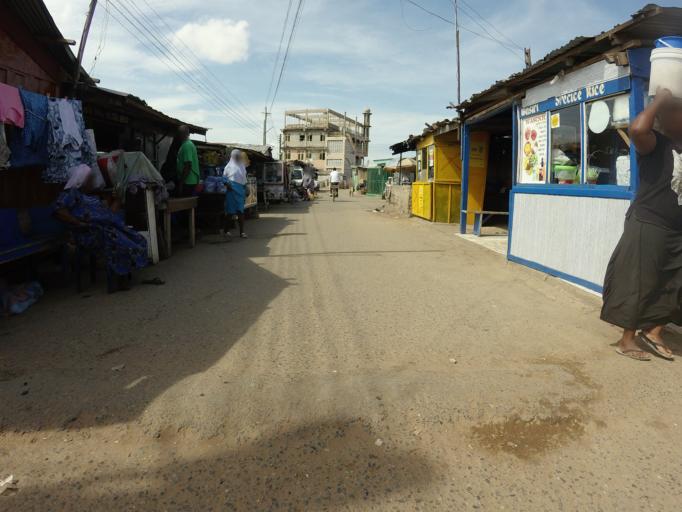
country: GH
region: Greater Accra
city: Accra
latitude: 5.5912
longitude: -0.1922
